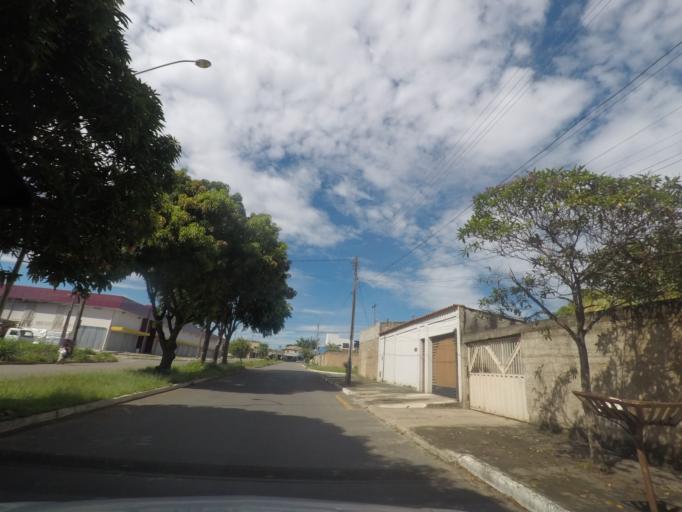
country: BR
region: Goias
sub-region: Aparecida De Goiania
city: Aparecida de Goiania
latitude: -16.8198
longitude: -49.2914
